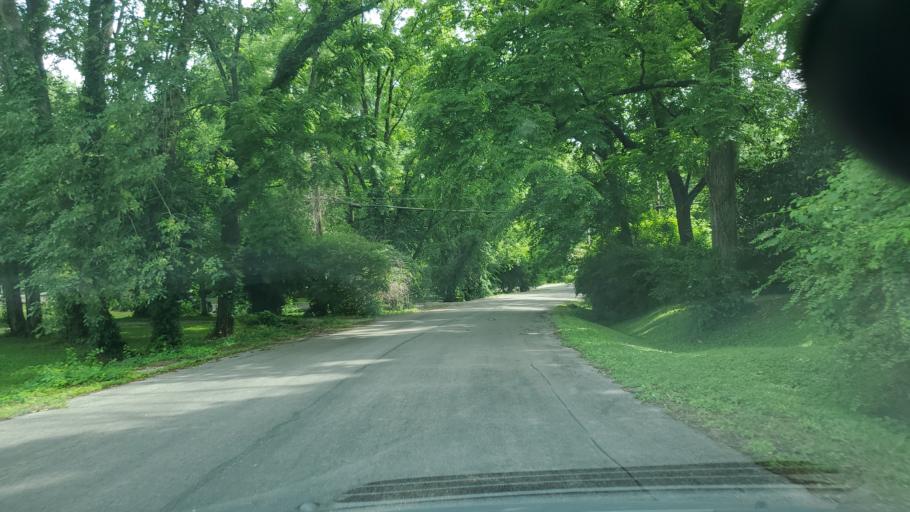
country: US
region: Tennessee
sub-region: Davidson County
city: Lakewood
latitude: 36.1998
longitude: -86.6811
